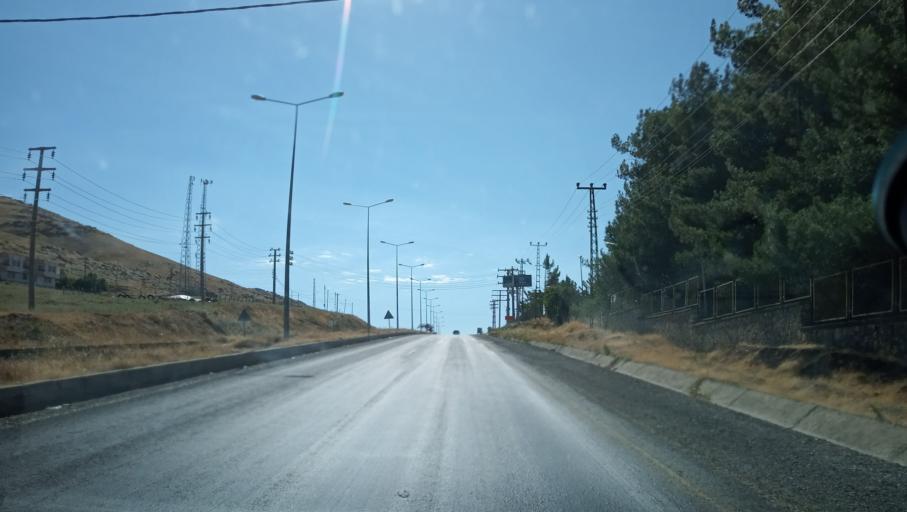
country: TR
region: Diyarbakir
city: Silvan
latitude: 38.1337
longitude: 41.0398
